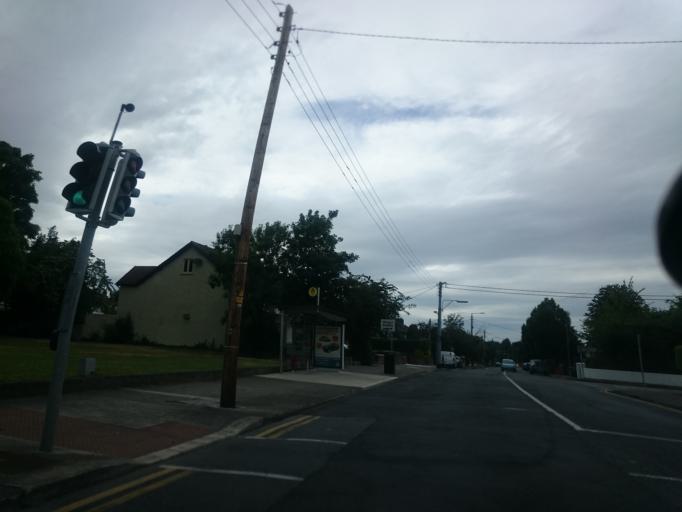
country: IE
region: Leinster
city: Templeogue
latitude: 53.3067
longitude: -6.3010
